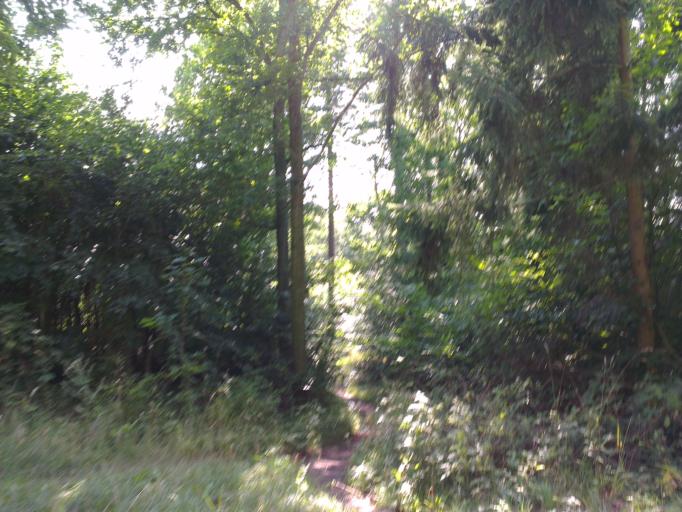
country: DK
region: Capital Region
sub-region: Frederikssund Kommune
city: Frederikssund
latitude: 55.8408
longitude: 12.0241
